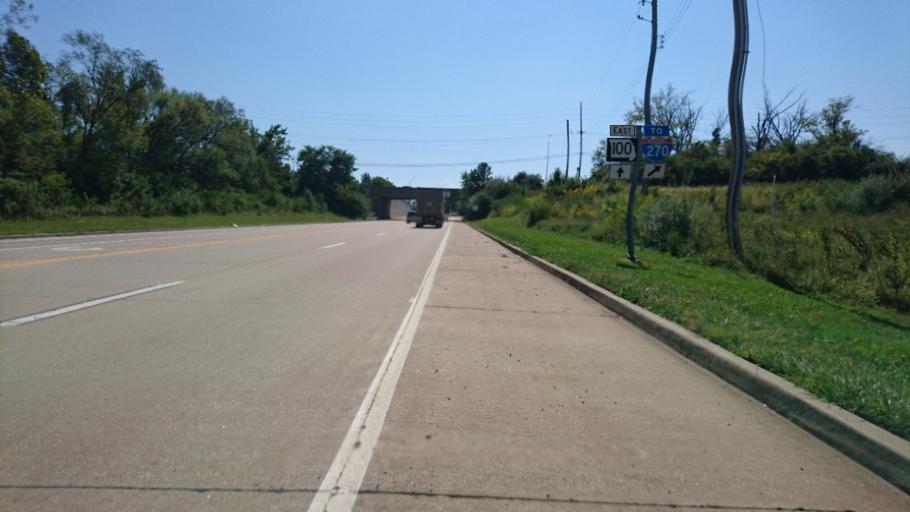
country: US
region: Missouri
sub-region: Saint Louis County
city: Town and Country
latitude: 38.6028
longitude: -90.4553
